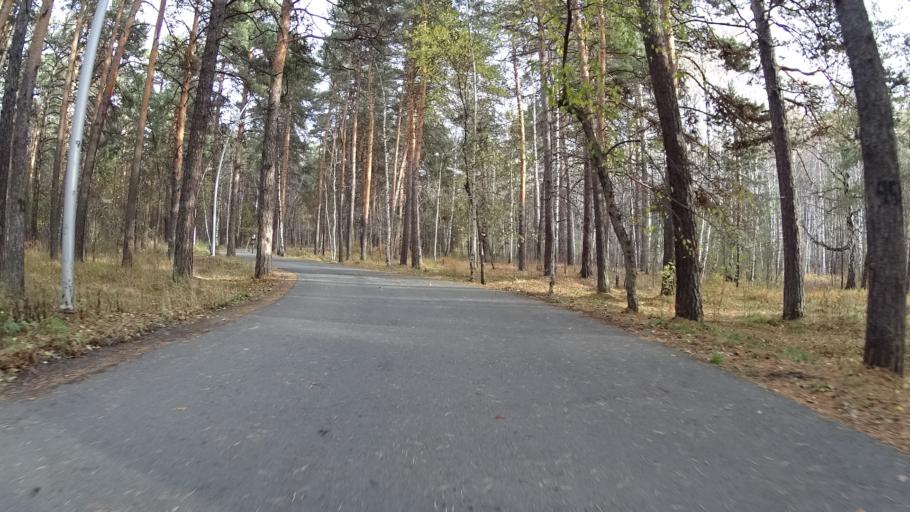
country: RU
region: Chelyabinsk
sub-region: Gorod Chelyabinsk
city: Chelyabinsk
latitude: 55.1399
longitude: 61.3495
